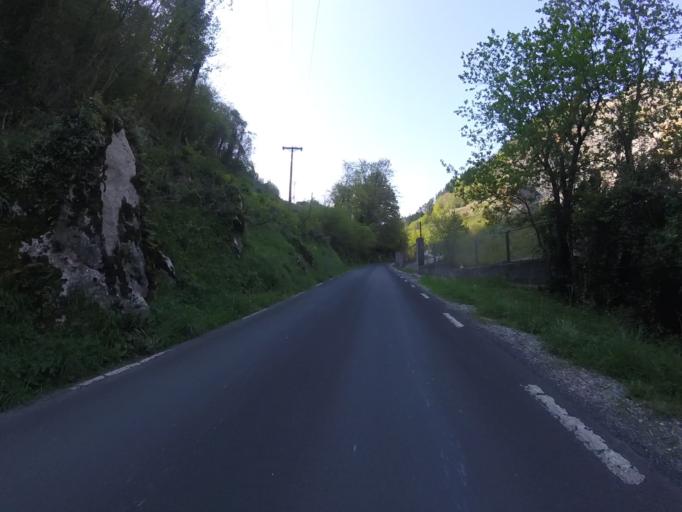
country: ES
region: Basque Country
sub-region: Provincia de Guipuzcoa
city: Azkoitia
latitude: 43.2379
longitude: -2.3234
